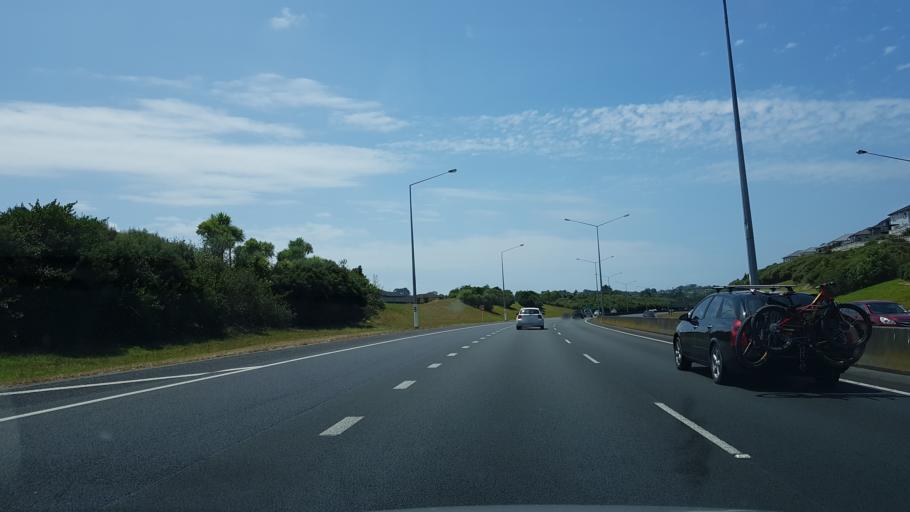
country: NZ
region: Auckland
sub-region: Auckland
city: Rothesay Bay
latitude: -36.7687
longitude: 174.6874
